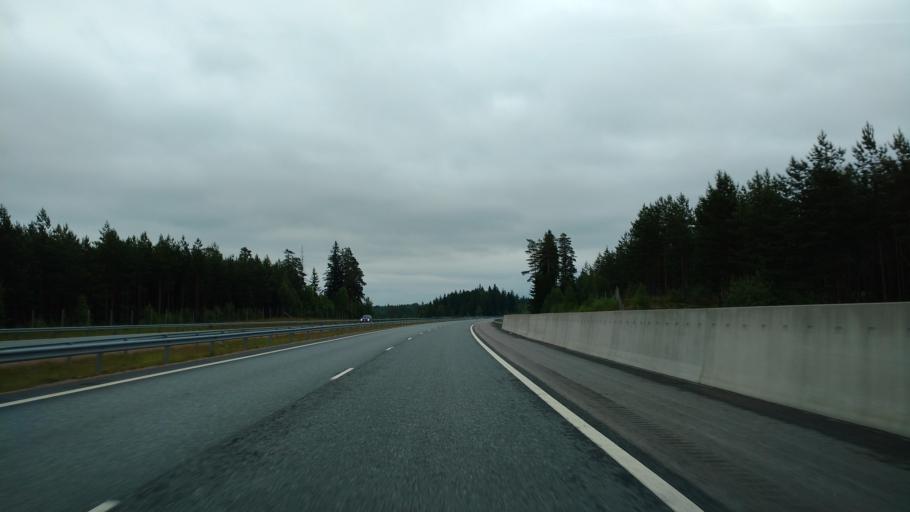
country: FI
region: Varsinais-Suomi
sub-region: Salo
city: Kiikala
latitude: 60.3900
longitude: 23.5150
